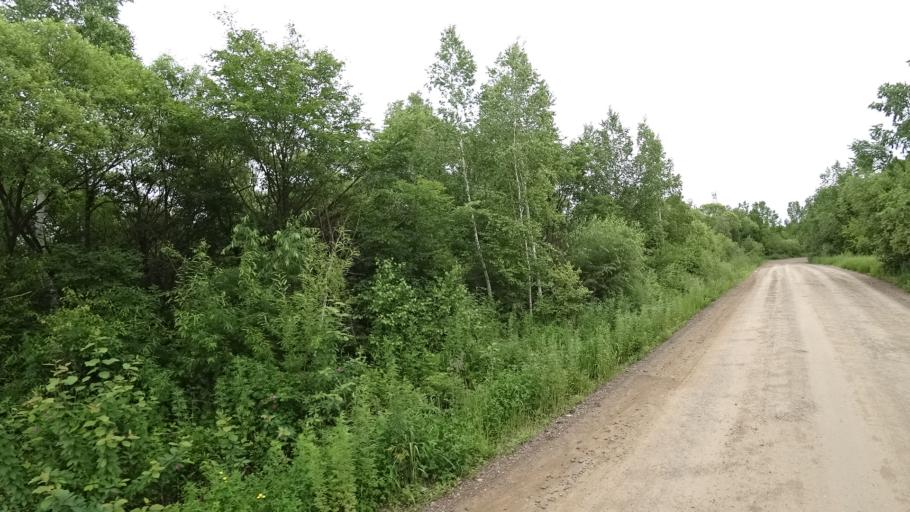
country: RU
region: Primorskiy
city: Arsen'yev
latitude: 44.1921
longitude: 133.3105
